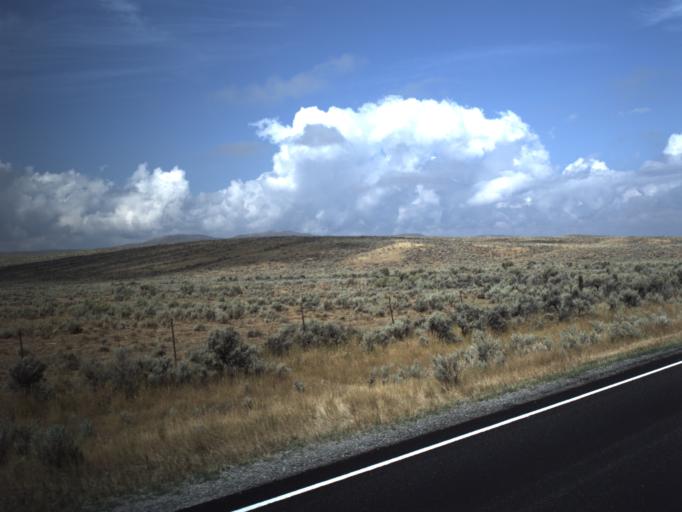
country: US
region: Utah
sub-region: Rich County
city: Randolph
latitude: 41.5688
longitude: -111.1605
